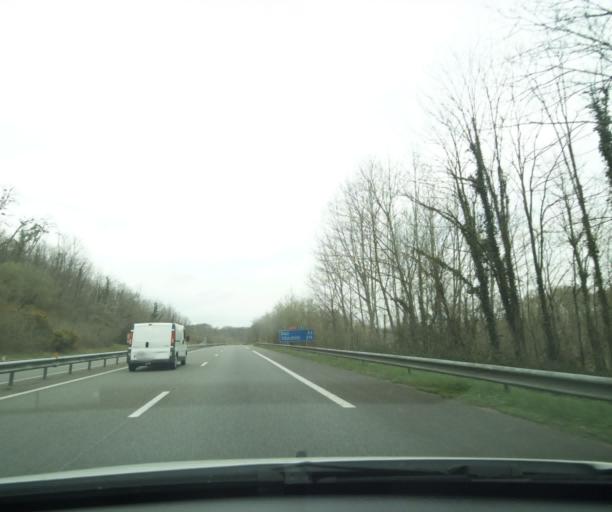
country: FR
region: Aquitaine
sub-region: Departement des Pyrenees-Atlantiques
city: Urt
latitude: 43.4746
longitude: -1.2798
